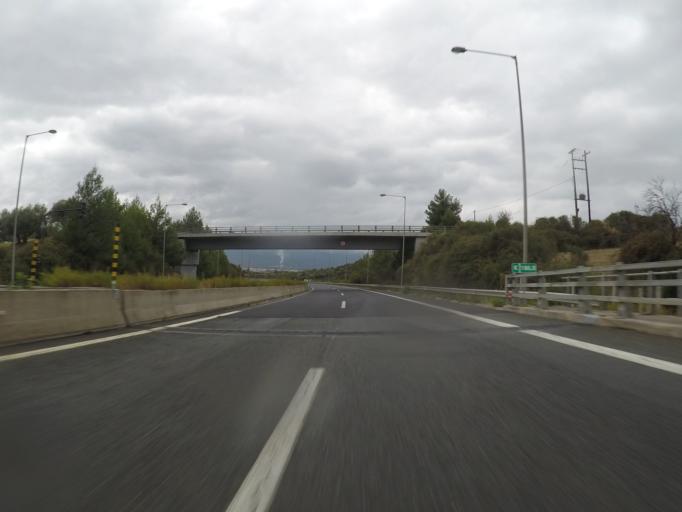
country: GR
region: Peloponnese
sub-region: Nomos Arkadias
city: Megalopoli
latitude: 37.3940
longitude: 22.1823
